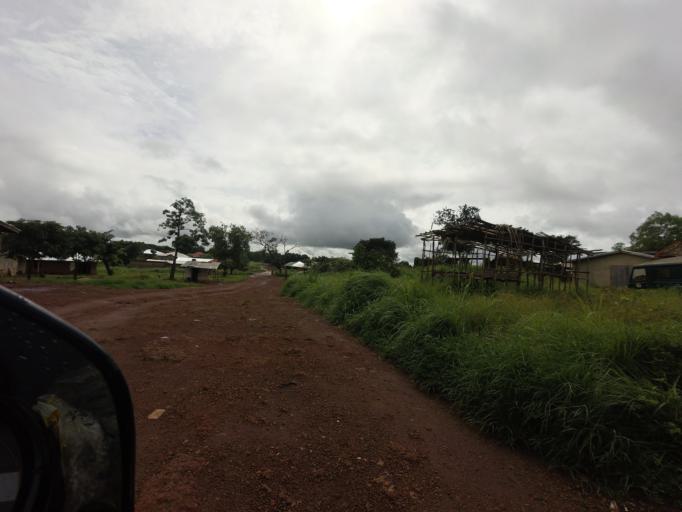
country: SL
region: Northern Province
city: Kambia
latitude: 9.1079
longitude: -12.9319
